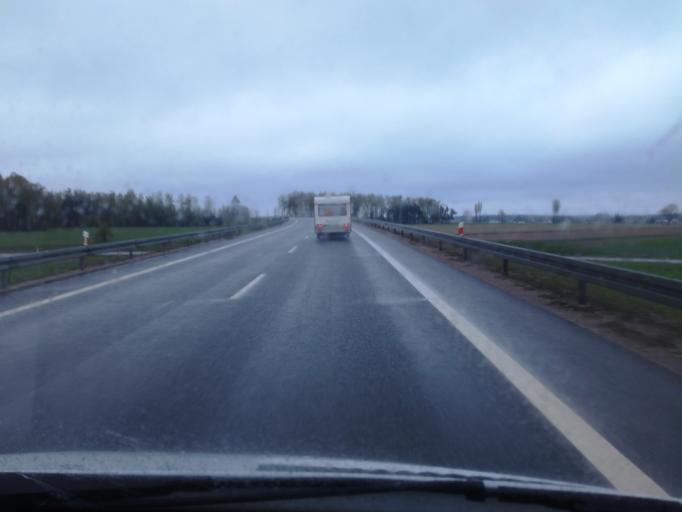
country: PL
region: Podlasie
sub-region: Powiat zambrowski
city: Zambrow
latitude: 52.9935
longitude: 22.2059
